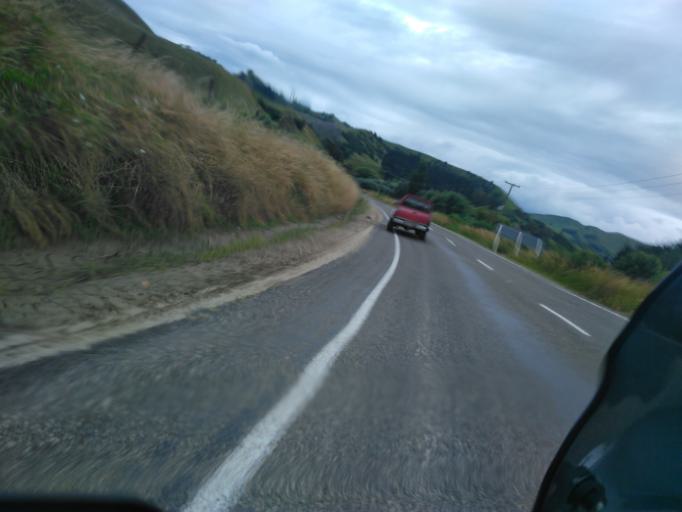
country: NZ
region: Gisborne
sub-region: Gisborne District
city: Gisborne
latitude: -38.4600
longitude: 177.7457
